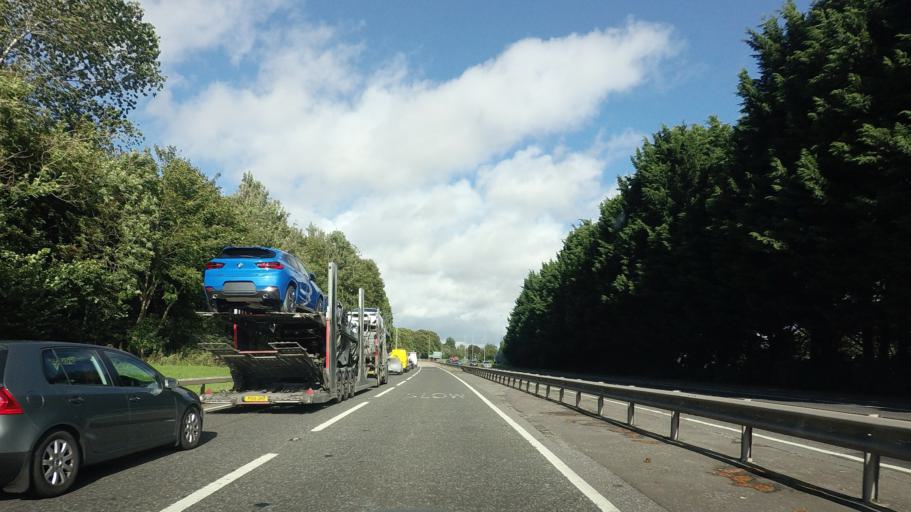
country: GB
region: Scotland
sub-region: Perth and Kinross
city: Luncarty
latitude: 56.4174
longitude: -3.4686
